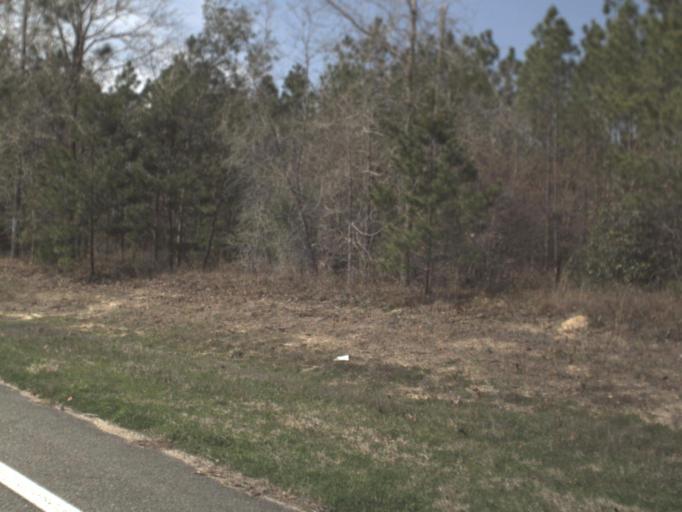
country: US
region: Florida
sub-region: Liberty County
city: Bristol
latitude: 30.5188
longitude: -84.8212
